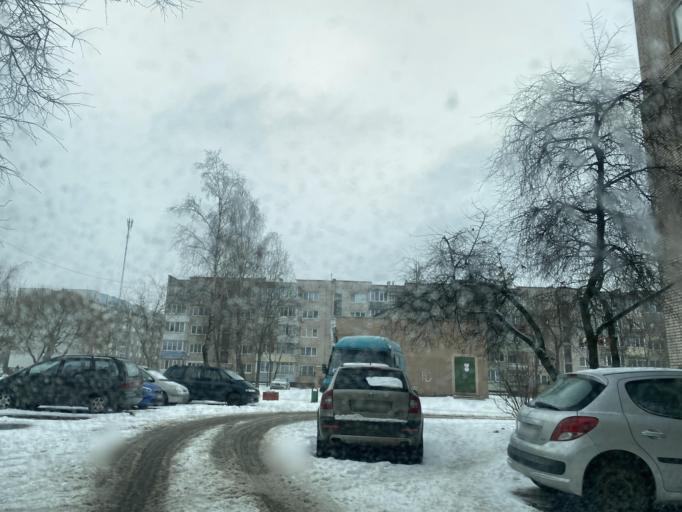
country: BY
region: Minsk
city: Horad Zhodzina
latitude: 54.0938
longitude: 28.3049
